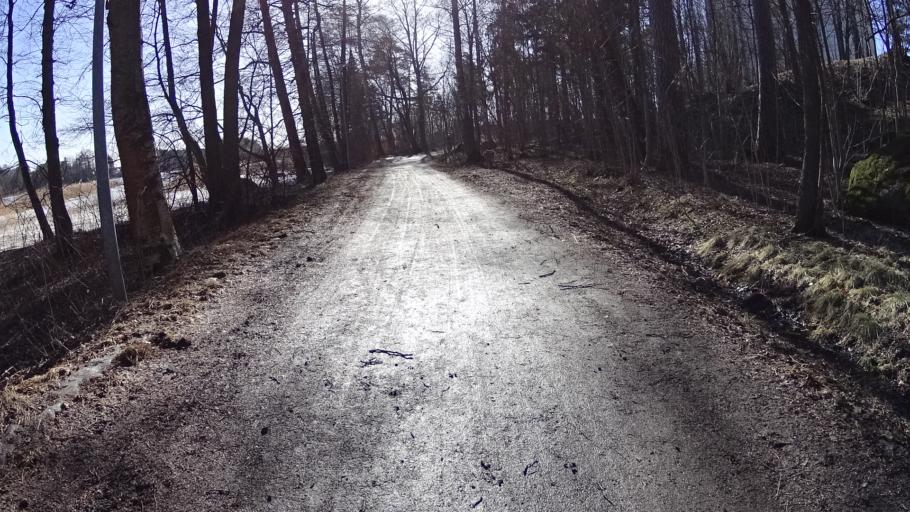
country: FI
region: Uusimaa
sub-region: Helsinki
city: Otaniemi
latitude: 60.1716
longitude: 24.8132
